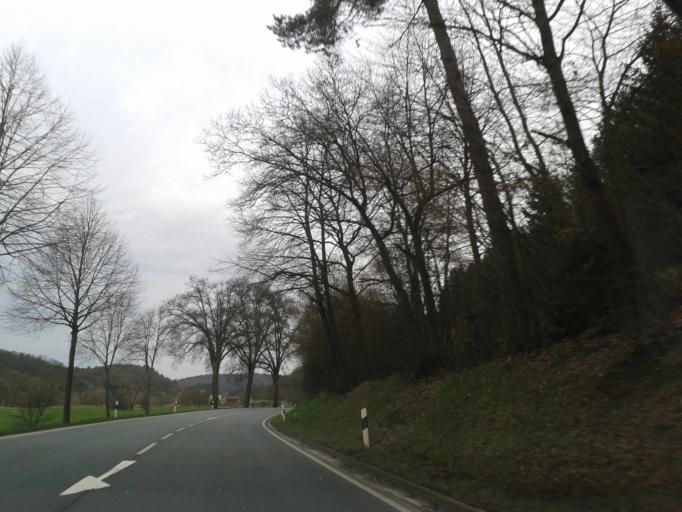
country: DE
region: Hesse
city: Frankenberg
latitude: 51.0750
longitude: 8.8162
